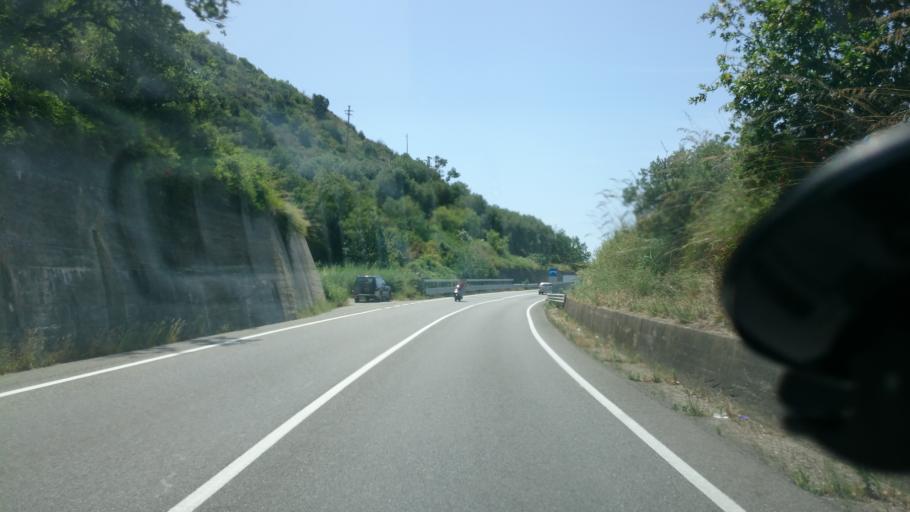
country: IT
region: Calabria
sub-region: Provincia di Cosenza
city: Cittadella del Capo
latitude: 39.5540
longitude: 15.8809
